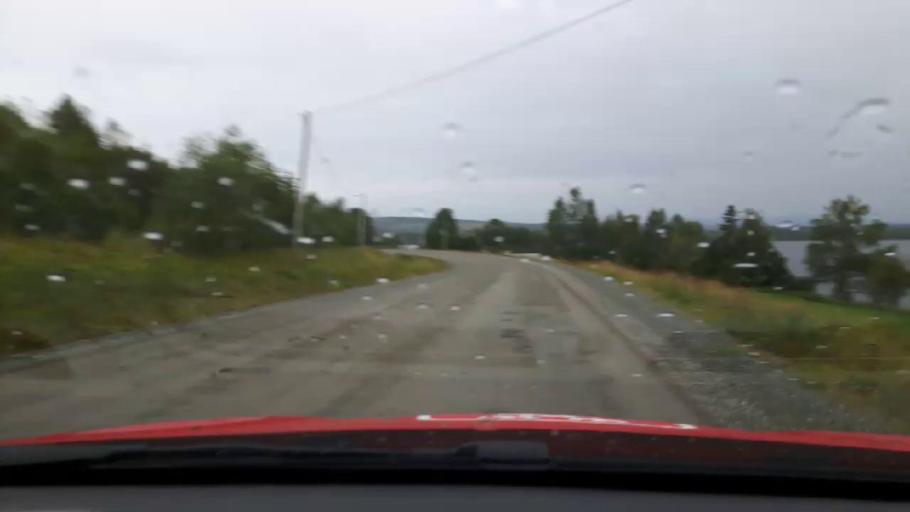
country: SE
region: Jaemtland
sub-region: Are Kommun
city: Are
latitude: 63.4604
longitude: 12.6359
